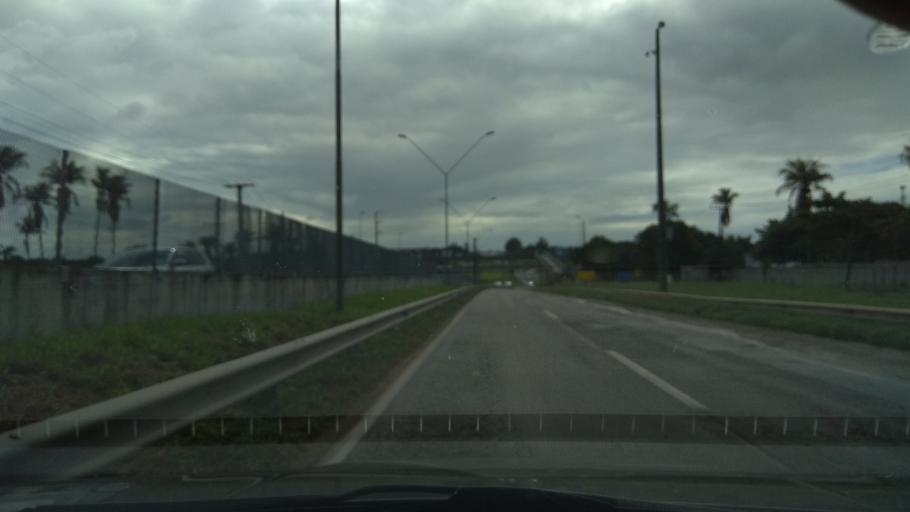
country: BR
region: Bahia
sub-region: Feira De Santana
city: Feira de Santana
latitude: -12.3023
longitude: -38.8959
